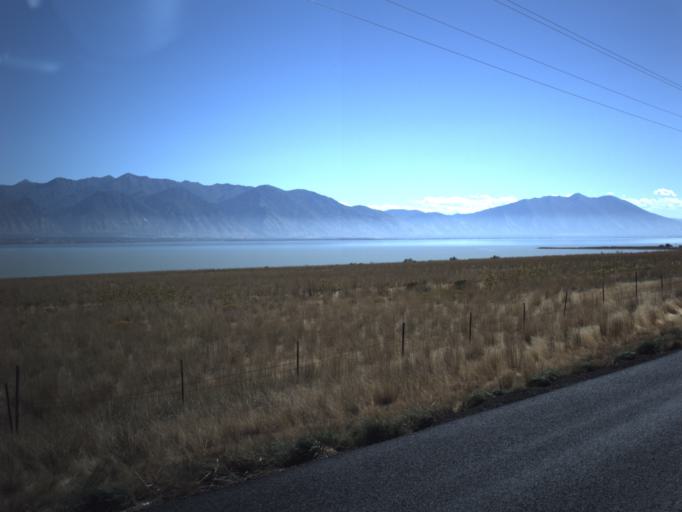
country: US
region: Utah
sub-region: Utah County
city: Saratoga Springs
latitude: 40.2804
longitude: -111.8712
